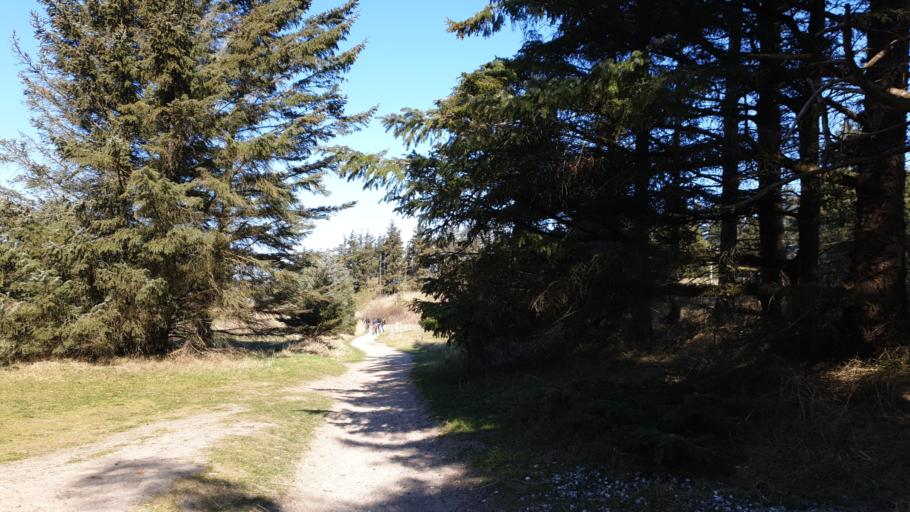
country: DK
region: North Denmark
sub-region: Hjorring Kommune
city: Hjorring
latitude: 57.4954
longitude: 9.8536
